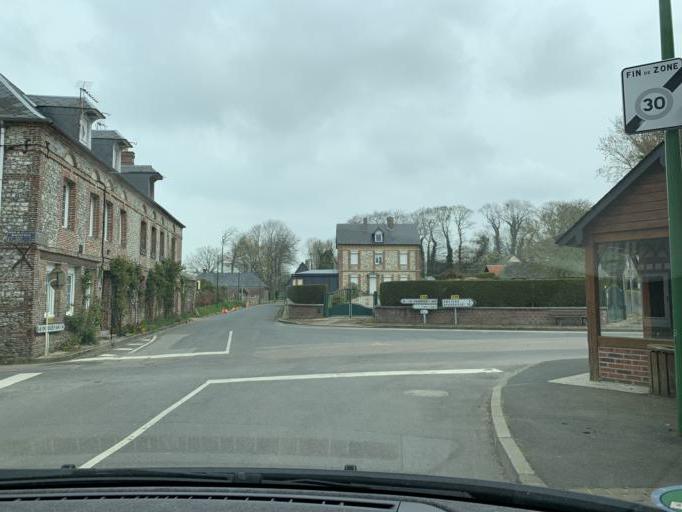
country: FR
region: Haute-Normandie
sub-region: Departement de la Seine-Maritime
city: Saint-Valery-en-Caux
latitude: 49.8544
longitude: 0.7935
